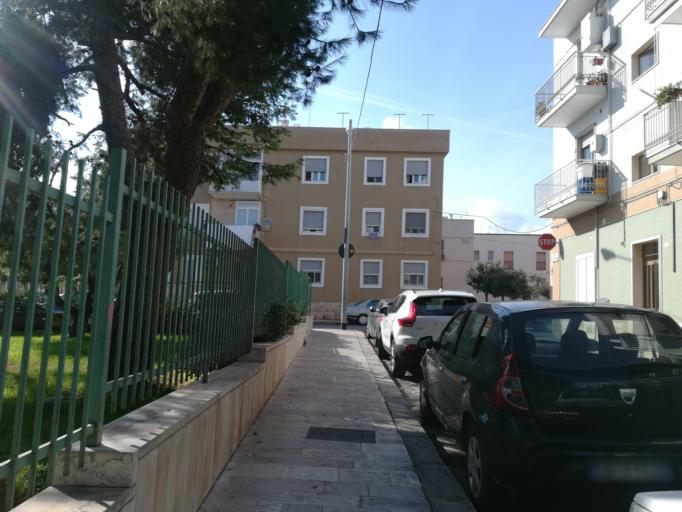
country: IT
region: Apulia
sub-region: Provincia di Bari
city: Polignano a Mare
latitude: 40.9921
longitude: 17.2204
